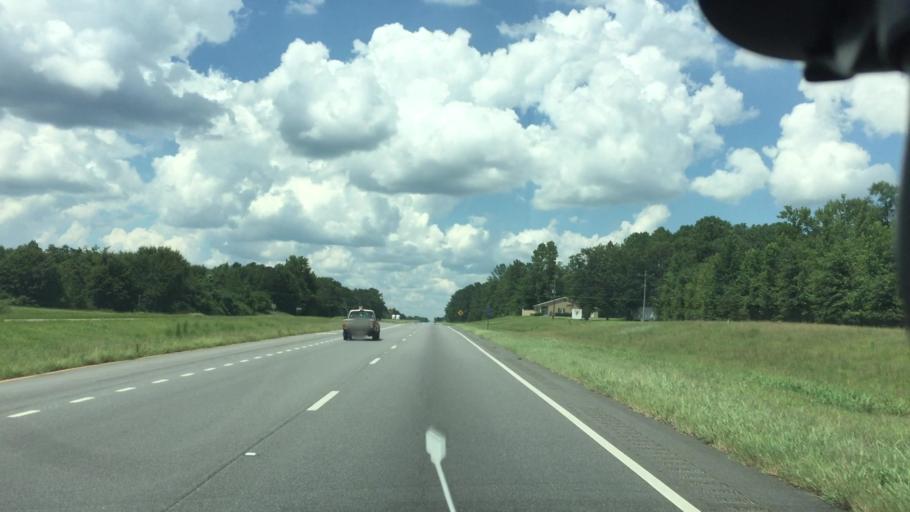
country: US
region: Alabama
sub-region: Pike County
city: Troy
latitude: 31.8743
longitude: -86.0022
